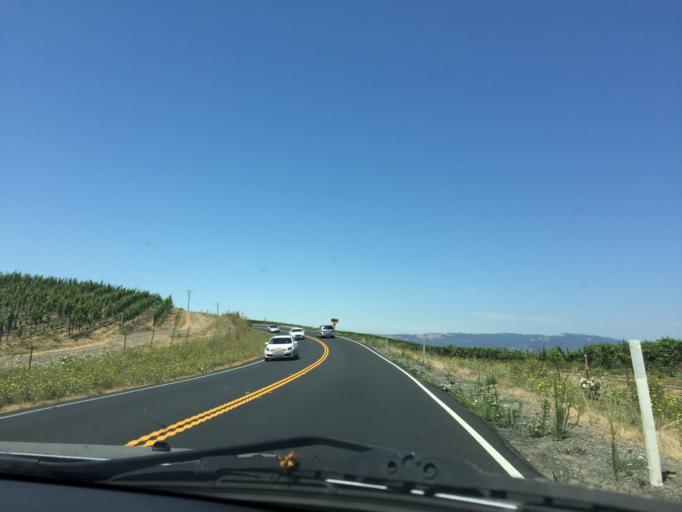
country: US
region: California
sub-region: Sonoma County
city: Sonoma
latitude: 38.2525
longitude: -122.4017
